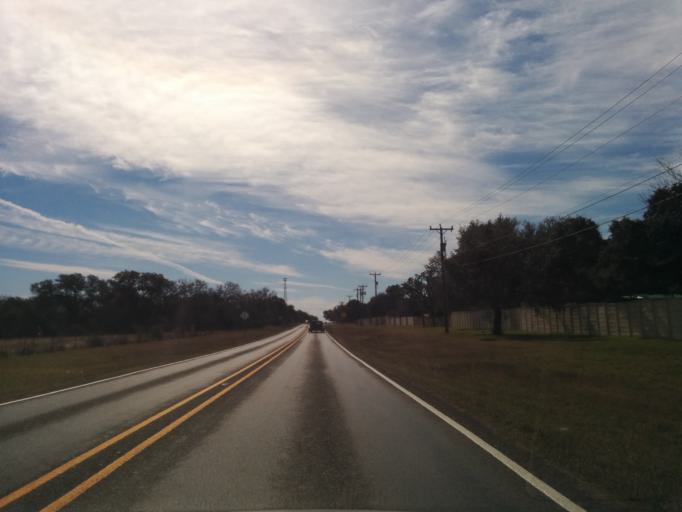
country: US
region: Texas
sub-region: Bexar County
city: Fair Oaks Ranch
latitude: 29.7418
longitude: -98.6233
